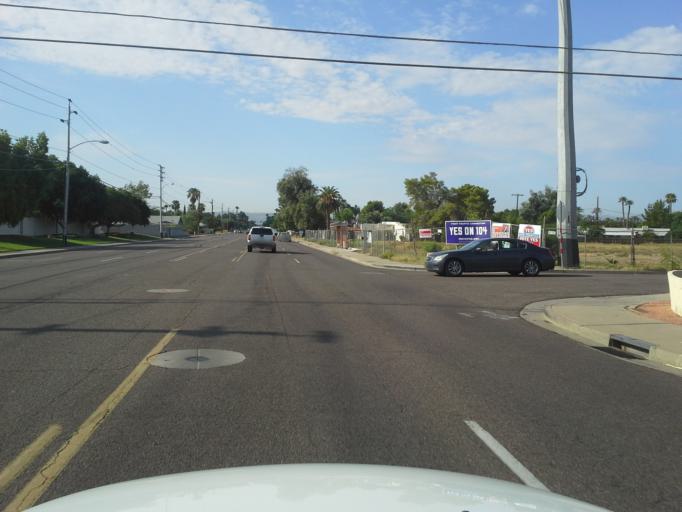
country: US
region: Arizona
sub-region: Maricopa County
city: Phoenix
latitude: 33.5349
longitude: -112.0476
